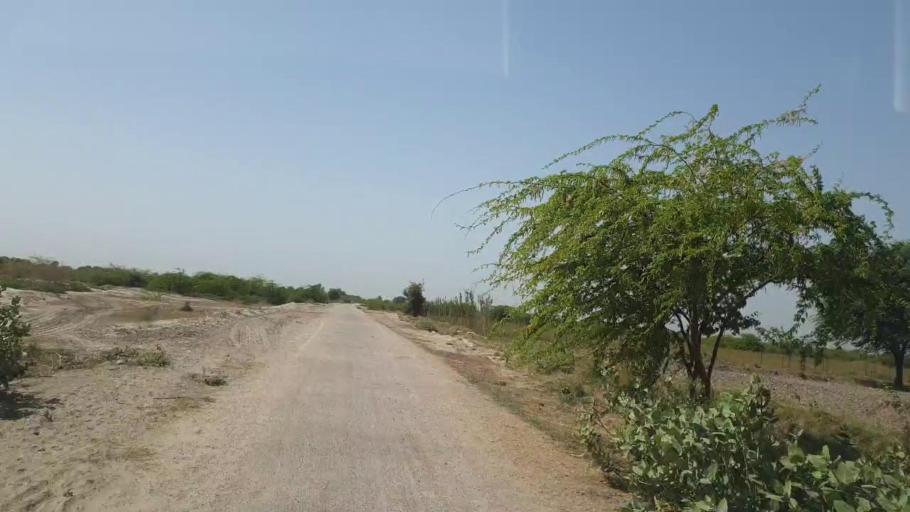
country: PK
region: Sindh
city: Naukot
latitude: 24.9568
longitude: 69.5134
